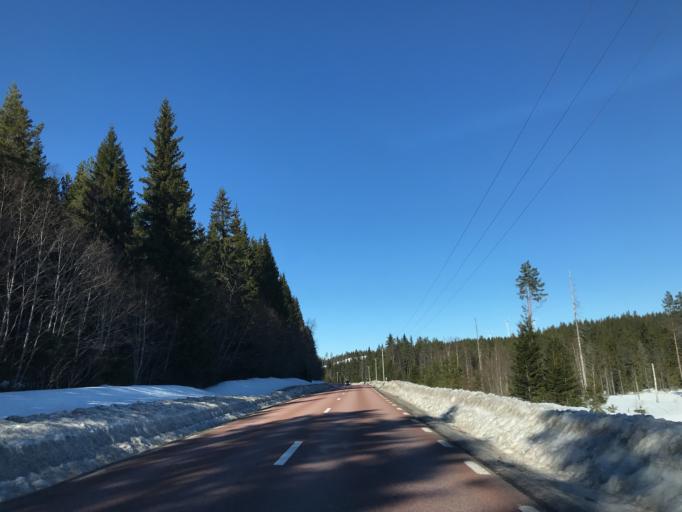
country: SE
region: Vaermland
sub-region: Filipstads Kommun
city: Lesjofors
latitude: 60.2168
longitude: 14.1870
